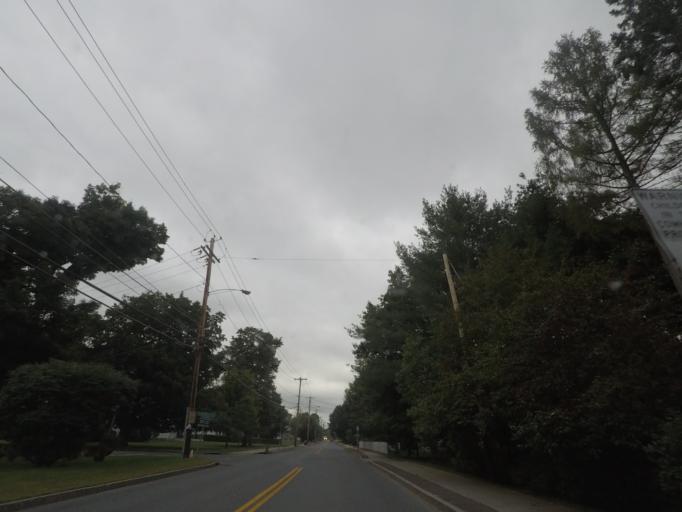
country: US
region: New York
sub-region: Rensselaer County
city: Hoosick Falls
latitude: 42.9094
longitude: -73.3512
